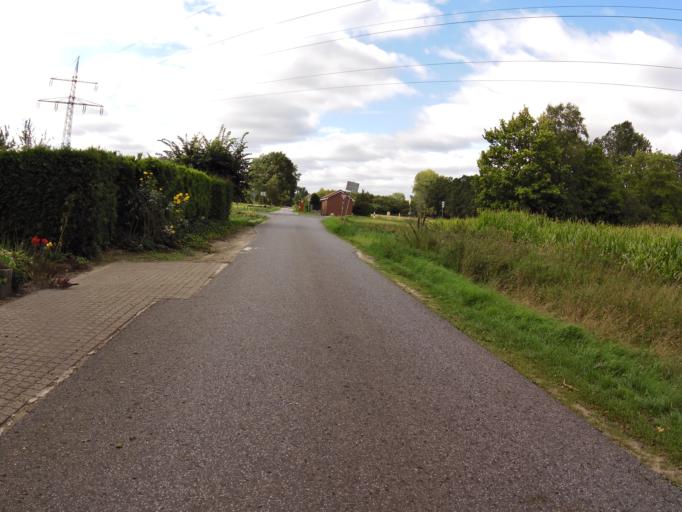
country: DE
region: North Rhine-Westphalia
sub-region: Regierungsbezirk Munster
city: Heek
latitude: 52.1639
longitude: 7.0694
